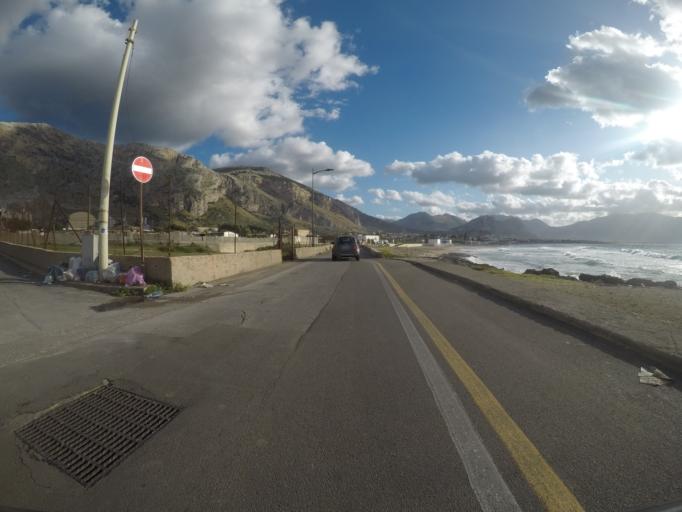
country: IT
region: Sicily
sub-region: Palermo
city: Isola delle Femmine
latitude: 38.1936
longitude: 13.2443
